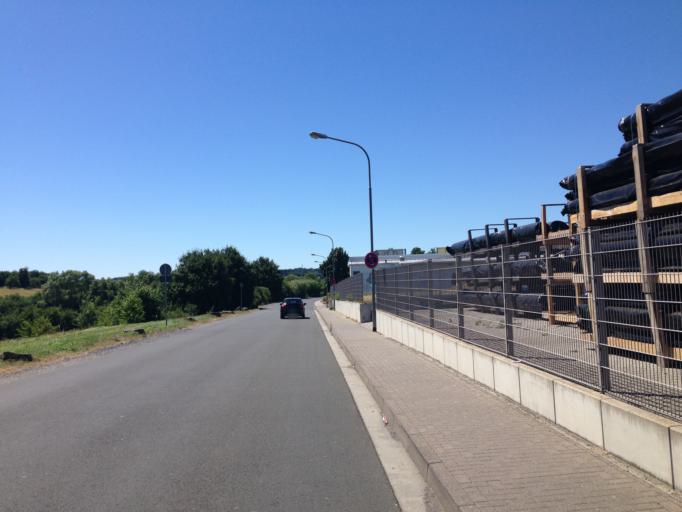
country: DE
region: Hesse
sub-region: Regierungsbezirk Giessen
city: Reiskirchen
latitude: 50.5954
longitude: 8.8212
